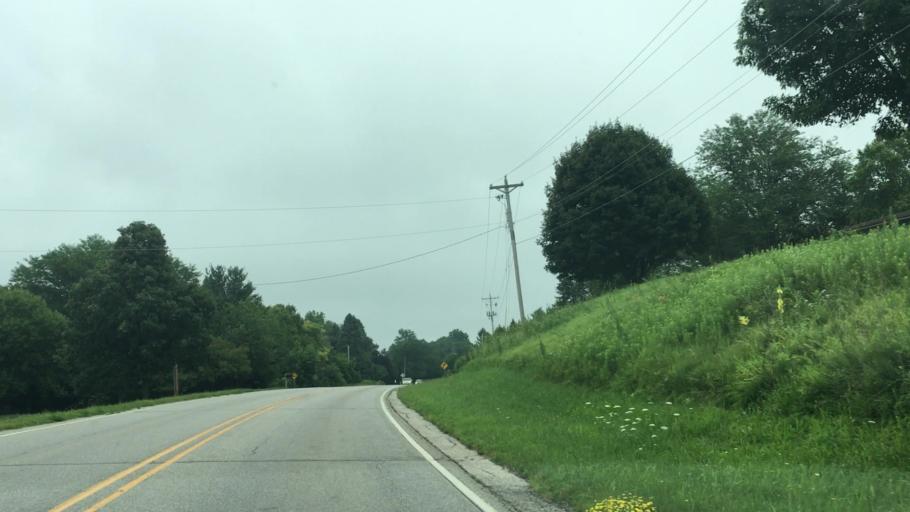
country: US
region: Iowa
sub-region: Johnson County
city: North Liberty
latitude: 41.7212
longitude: -91.5582
